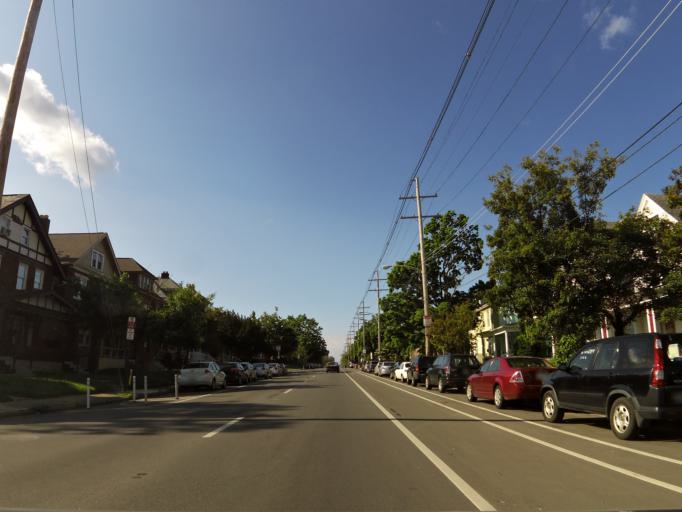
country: US
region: Ohio
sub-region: Franklin County
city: Columbus
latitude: 39.9943
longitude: -83.0016
